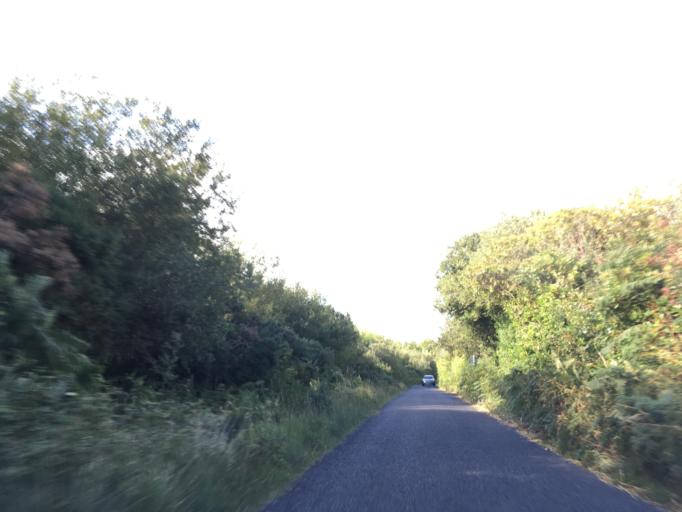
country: IE
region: Munster
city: Cahir
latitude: 52.2624
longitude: -7.9618
